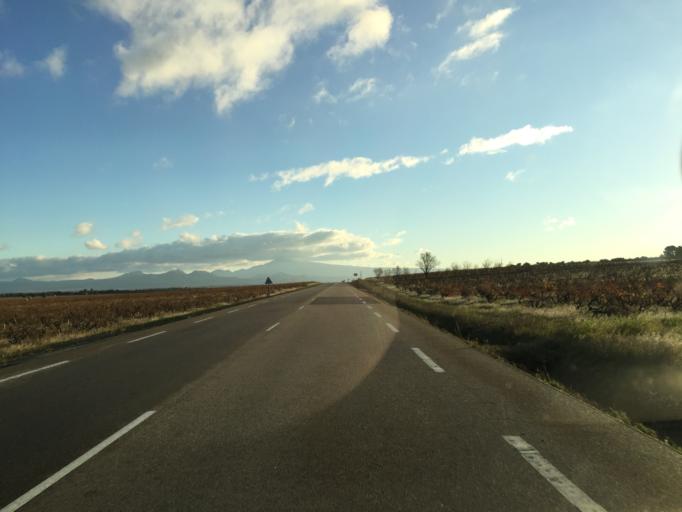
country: FR
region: Provence-Alpes-Cote d'Azur
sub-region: Departement du Vaucluse
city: Chateauneuf-du-Pape
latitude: 44.0961
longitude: 4.8402
